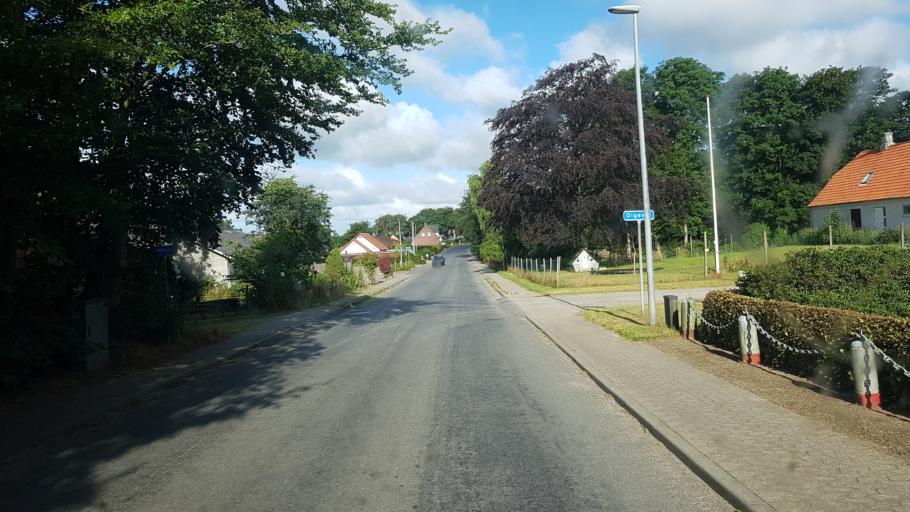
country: DK
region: South Denmark
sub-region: Vejen Kommune
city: Holsted
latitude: 55.4473
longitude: 8.8804
